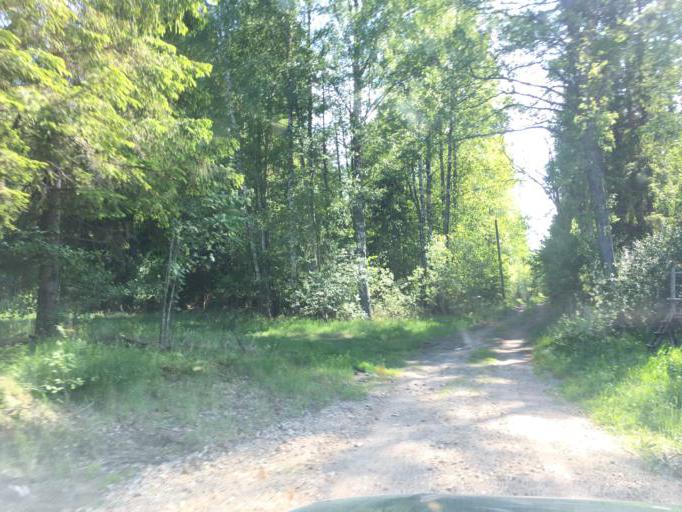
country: LV
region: Dundaga
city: Dundaga
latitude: 57.6044
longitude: 22.5106
